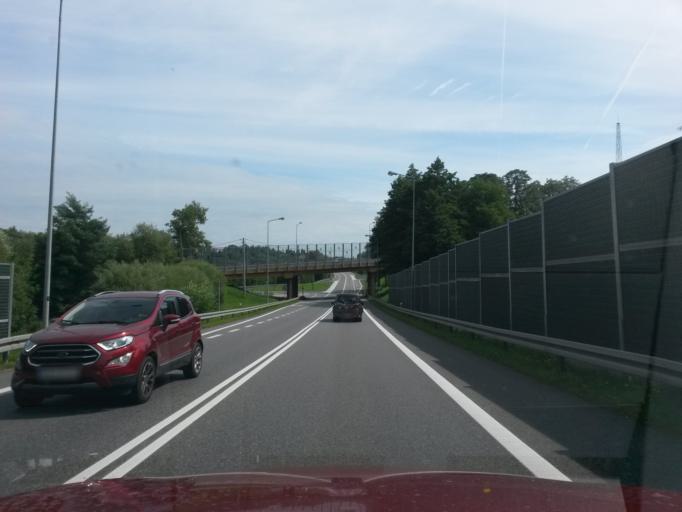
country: PL
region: Lesser Poland Voivodeship
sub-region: Powiat bochenski
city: Bochnia
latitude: 49.9579
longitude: 20.4257
